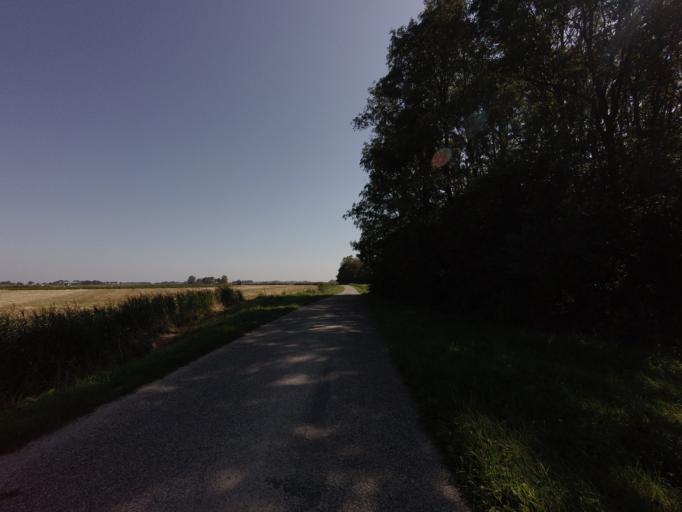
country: NL
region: Friesland
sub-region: Gemeente Dongeradeel
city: Holwerd
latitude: 53.3676
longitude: 5.9128
